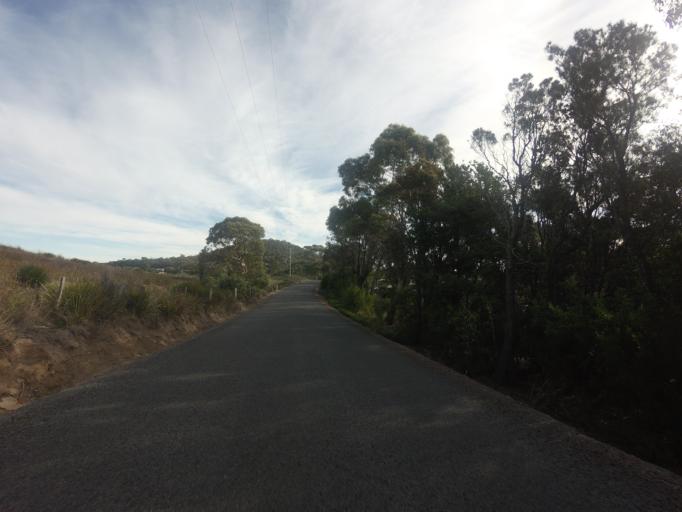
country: AU
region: Tasmania
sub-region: Sorell
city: Sorell
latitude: -42.9635
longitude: 147.8345
